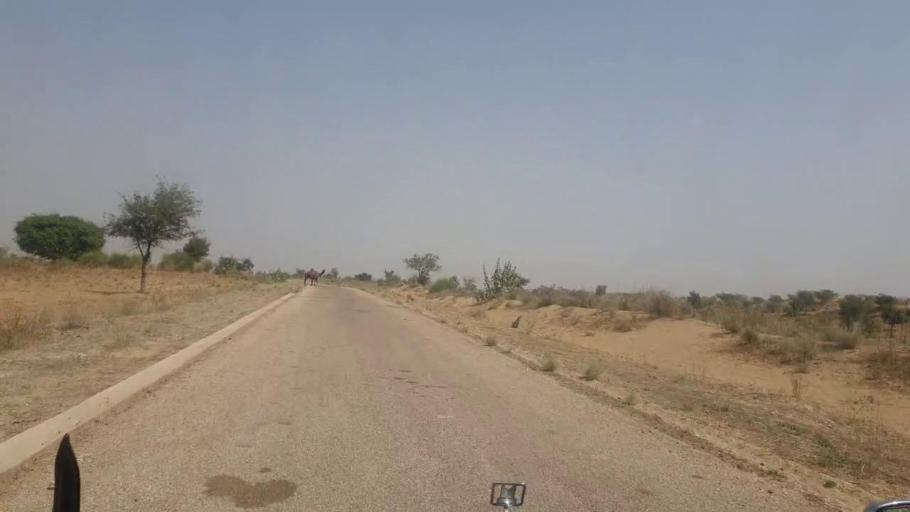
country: PK
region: Sindh
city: Umarkot
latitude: 25.2219
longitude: 70.2391
